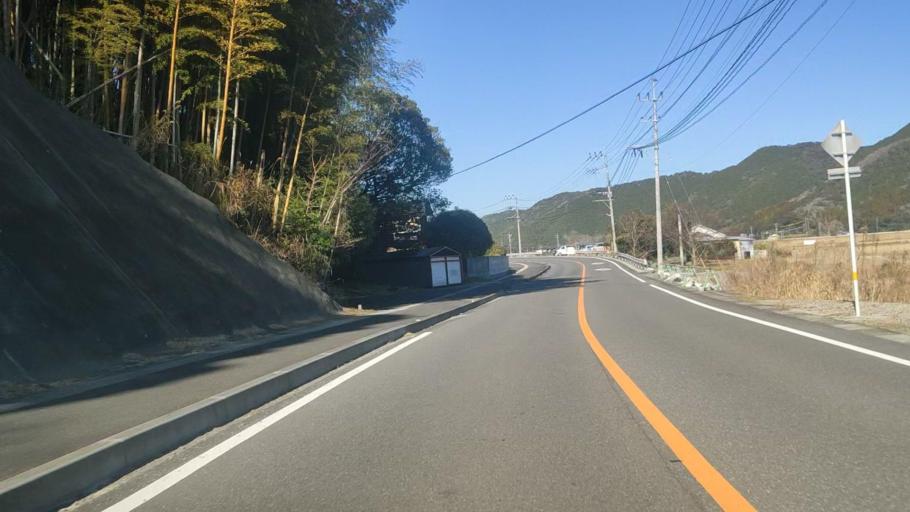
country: JP
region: Oita
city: Saiki
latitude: 32.9264
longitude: 131.9230
